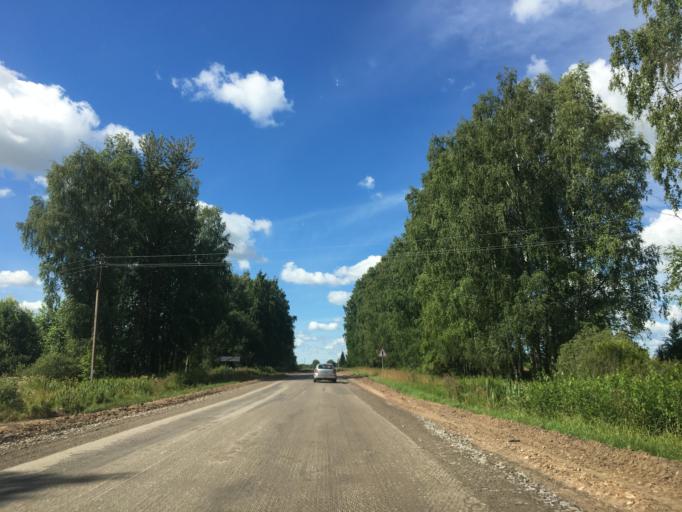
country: RU
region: Pskov
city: Palkino
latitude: 57.5524
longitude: 28.0539
